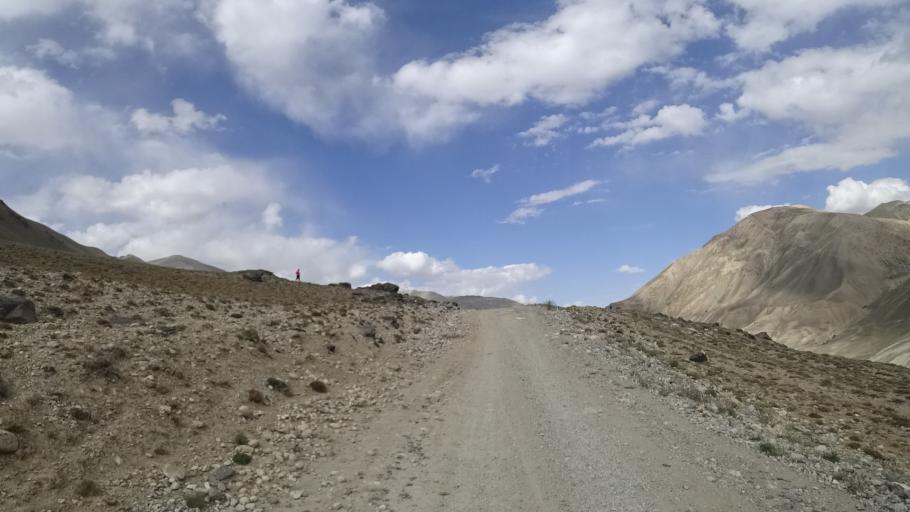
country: AF
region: Badakhshan
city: Khandud
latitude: 37.1985
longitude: 72.7724
